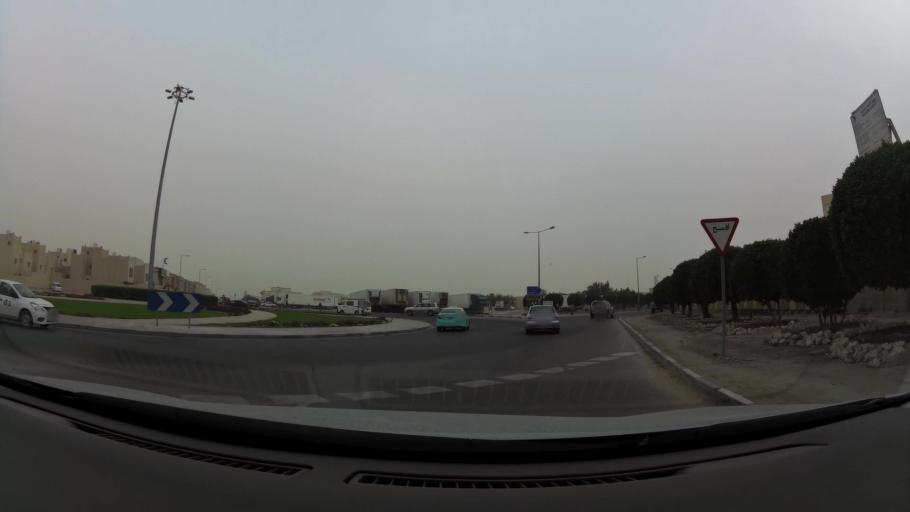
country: QA
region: Baladiyat ad Dawhah
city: Doha
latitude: 25.2467
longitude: 51.4788
